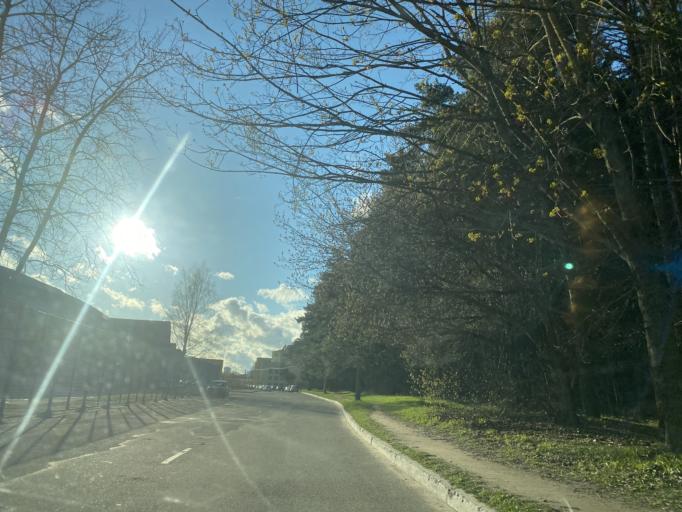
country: BY
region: Minsk
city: Borovlyany
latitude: 53.9455
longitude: 27.6523
